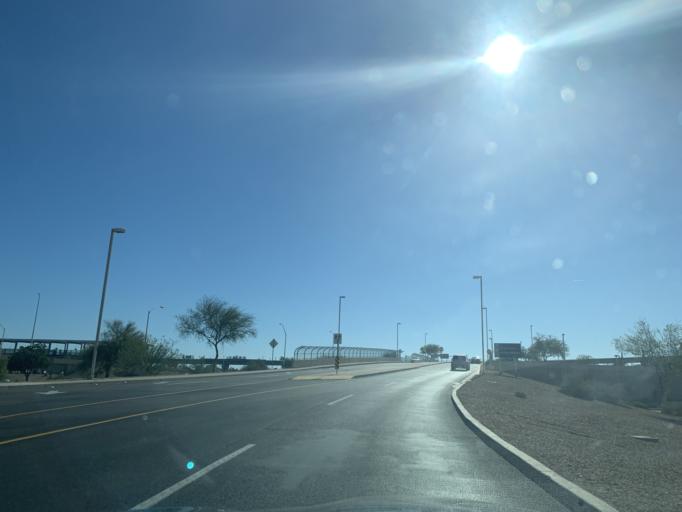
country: US
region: Arizona
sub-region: Maricopa County
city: Tempe Junction
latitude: 33.4368
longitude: -111.9879
